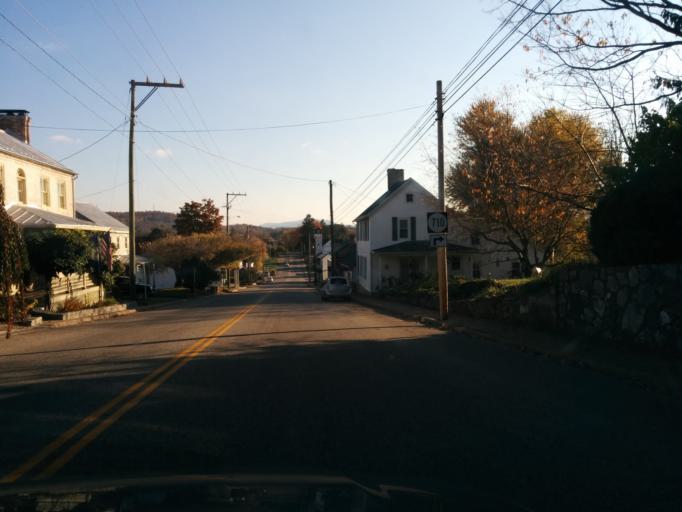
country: US
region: Virginia
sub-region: City of Buena Vista
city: Buena Vista
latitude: 37.8791
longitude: -79.2905
